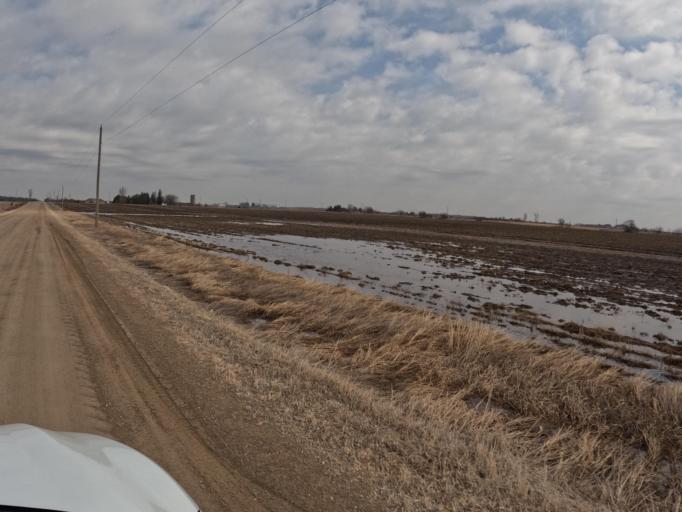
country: CA
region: Ontario
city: Orangeville
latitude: 43.9166
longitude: -80.2170
